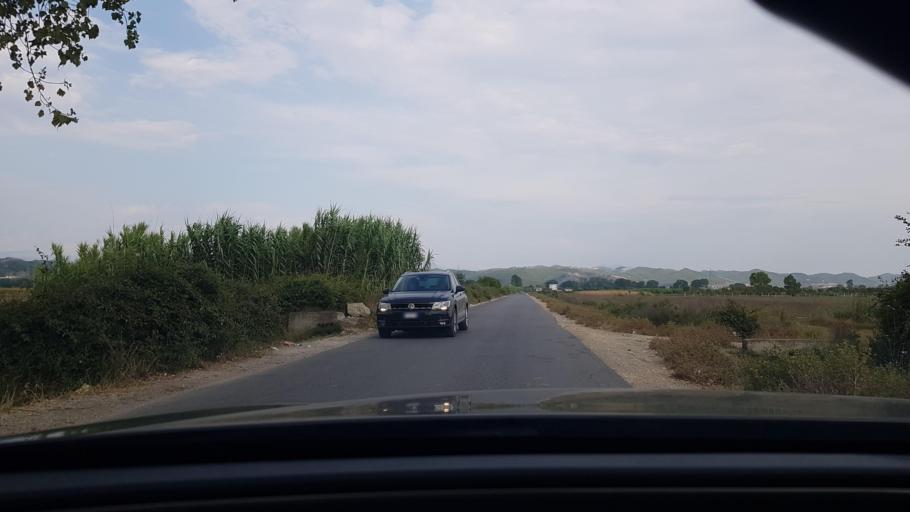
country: AL
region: Durres
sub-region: Rrethi i Durresit
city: Katundi i Ri
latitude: 41.4841
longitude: 19.5310
